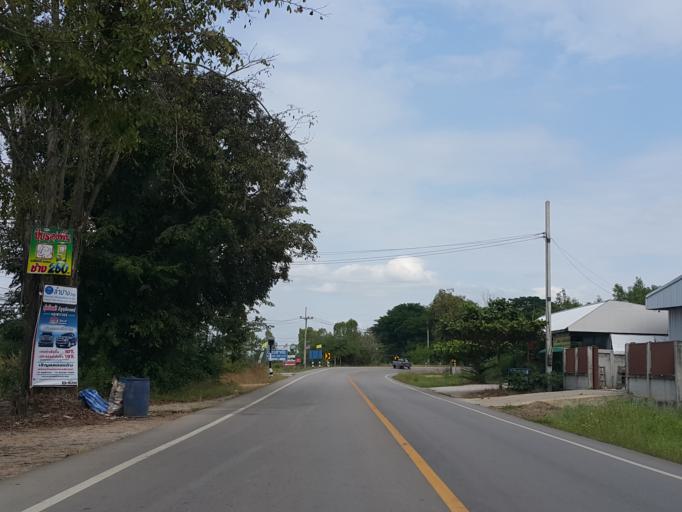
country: TH
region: Lampang
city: Lampang
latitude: 18.3167
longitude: 99.4633
